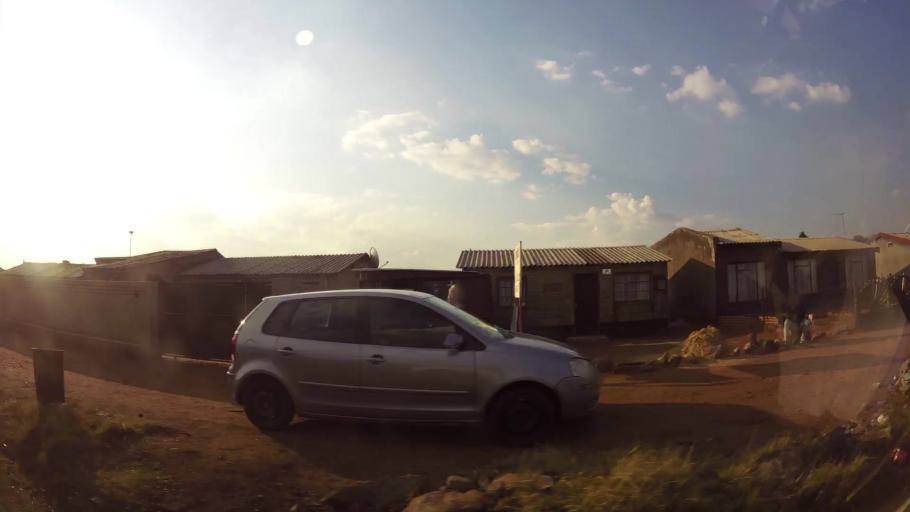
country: ZA
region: Gauteng
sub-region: Ekurhuleni Metropolitan Municipality
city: Germiston
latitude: -26.3475
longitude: 28.2108
